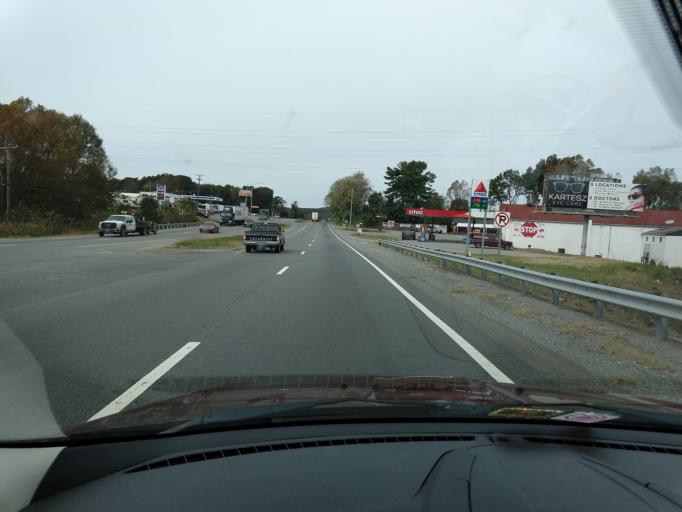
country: US
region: Virginia
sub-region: Franklin County
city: Rocky Mount
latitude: 37.0441
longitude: -79.8766
